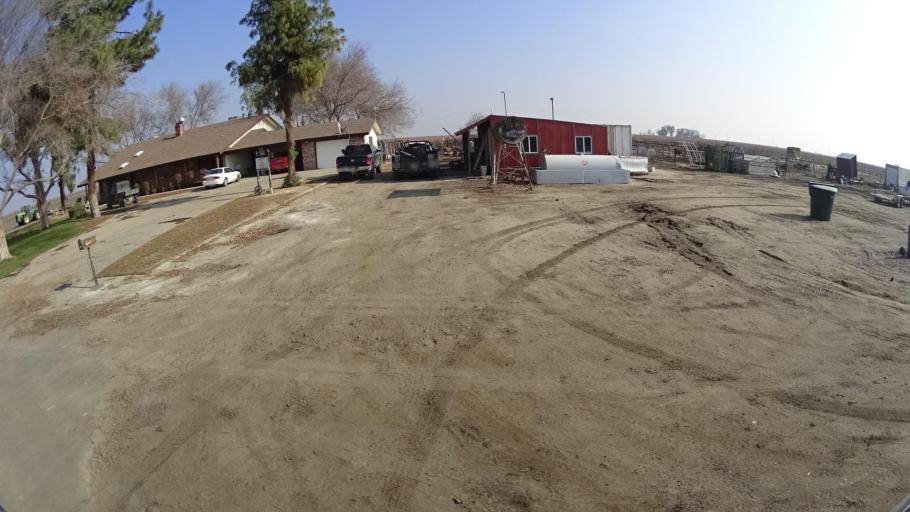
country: US
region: California
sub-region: Kern County
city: Buttonwillow
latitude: 35.3577
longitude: -119.4122
